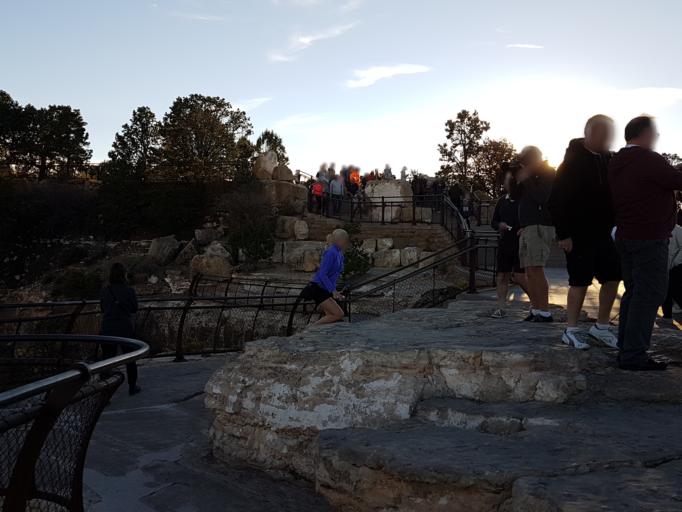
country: US
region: Arizona
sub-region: Coconino County
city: Grand Canyon
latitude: 36.0615
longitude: -112.1077
